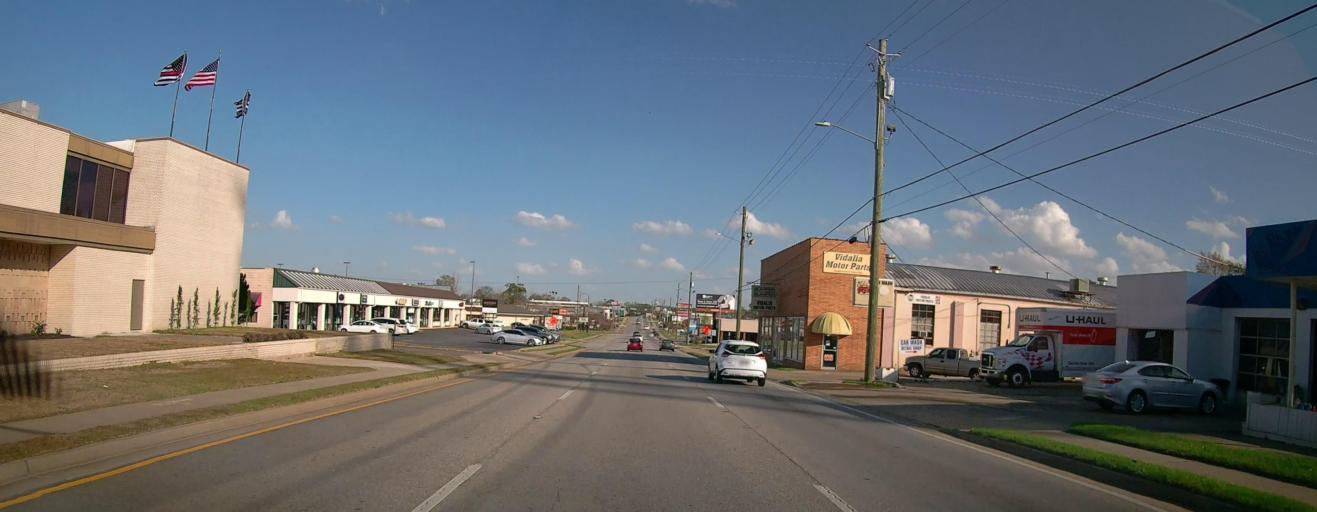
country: US
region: Georgia
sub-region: Toombs County
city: Vidalia
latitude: 32.2163
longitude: -82.4102
